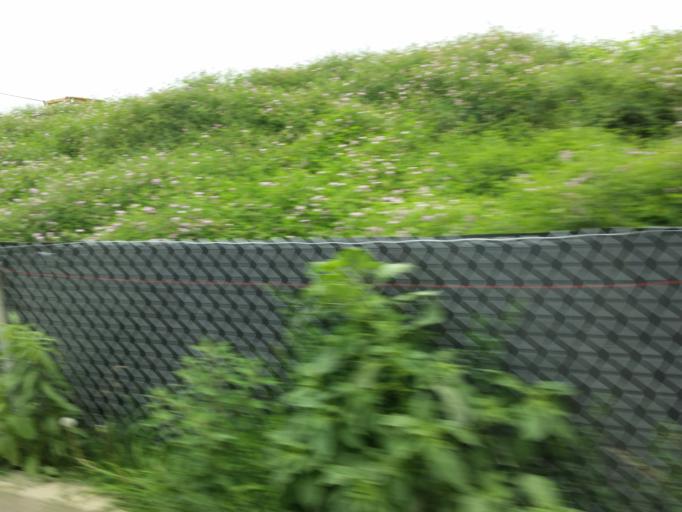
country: US
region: Pennsylvania
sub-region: York County
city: North York
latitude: 39.9912
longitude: -76.7425
